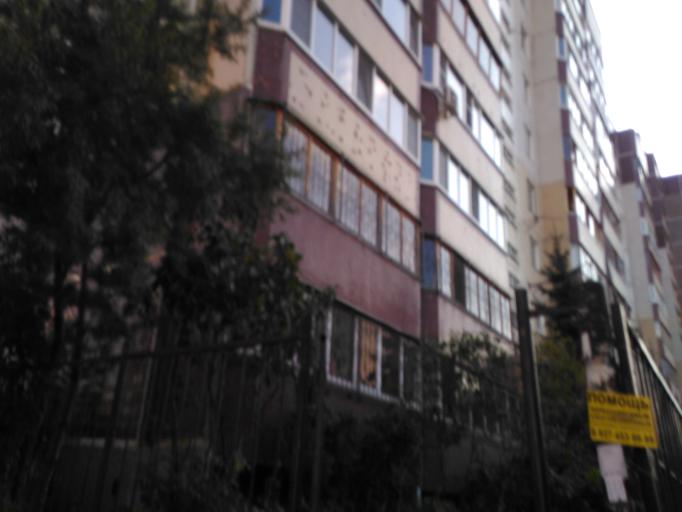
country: RU
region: Ulyanovsk
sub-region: Ulyanovskiy Rayon
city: Ulyanovsk
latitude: 54.3330
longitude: 48.3896
